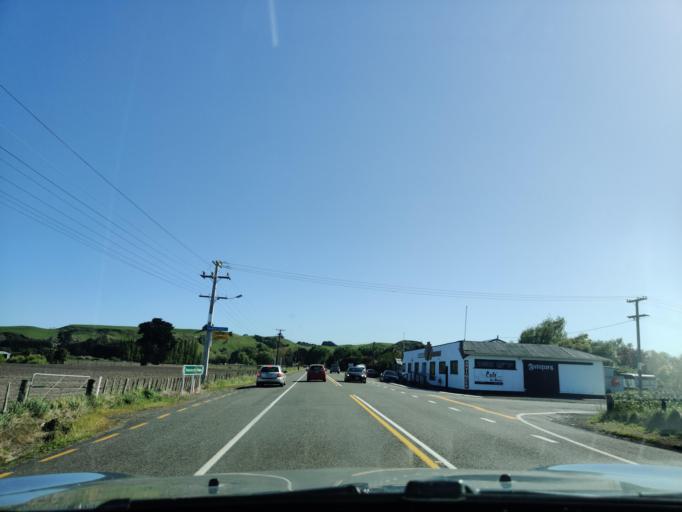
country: NZ
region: Manawatu-Wanganui
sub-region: Wanganui District
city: Wanganui
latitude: -40.0395
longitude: 175.2120
